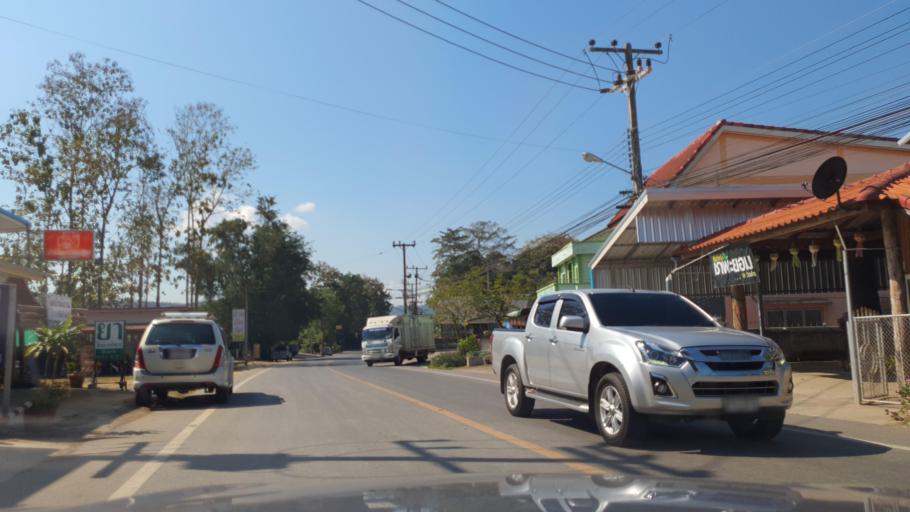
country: TH
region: Nan
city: Tha Wang Pha
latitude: 19.0820
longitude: 100.8871
